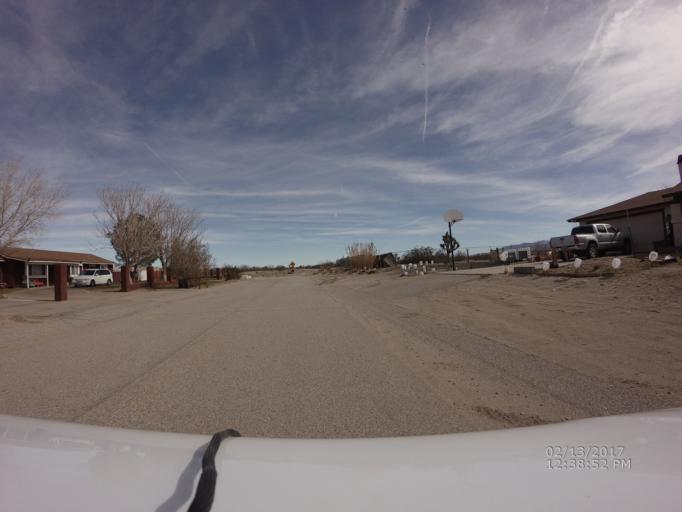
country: US
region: California
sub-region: Los Angeles County
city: Littlerock
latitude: 34.5707
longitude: -117.9191
